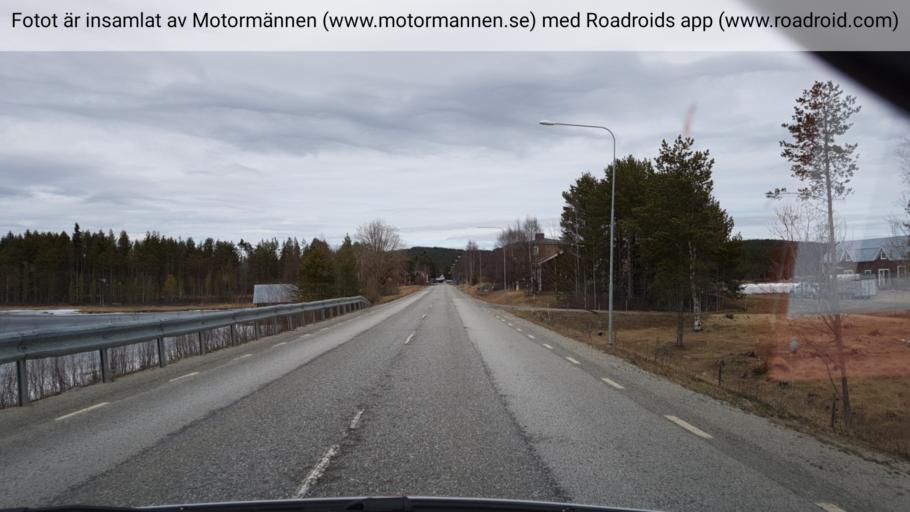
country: SE
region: Vaesterbotten
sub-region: Asele Kommun
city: Asele
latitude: 63.9347
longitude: 17.2729
